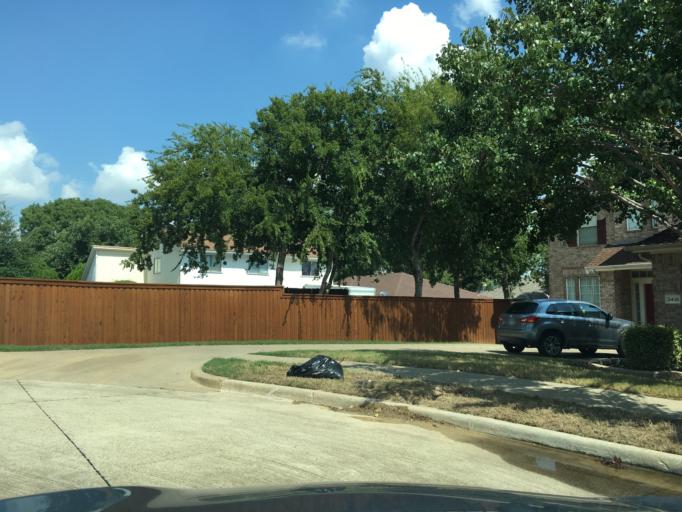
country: US
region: Texas
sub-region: Dallas County
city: Garland
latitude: 32.9476
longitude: -96.6386
